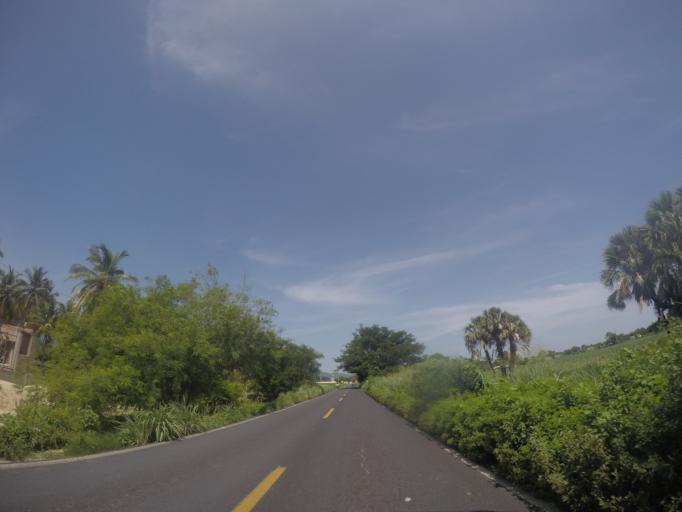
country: MX
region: Oaxaca
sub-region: Villa de Tututepec de Melchor Ocampo
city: Santa Rosa de Lima
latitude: 16.0114
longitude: -97.4558
